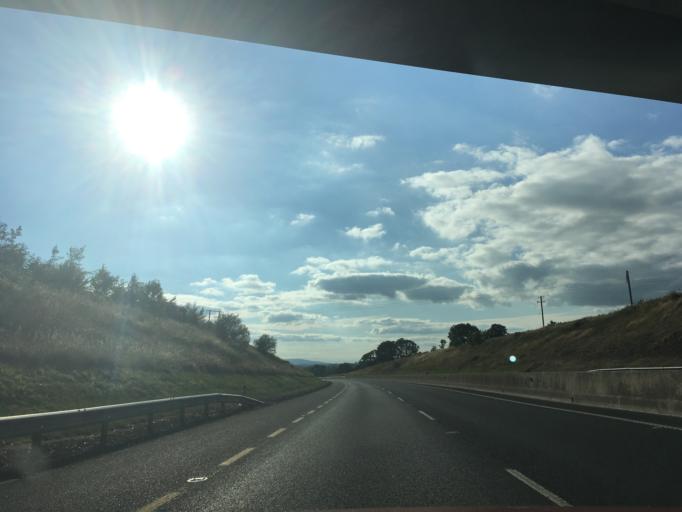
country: IE
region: Munster
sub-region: Waterford
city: Waterford
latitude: 52.2890
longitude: -7.1014
